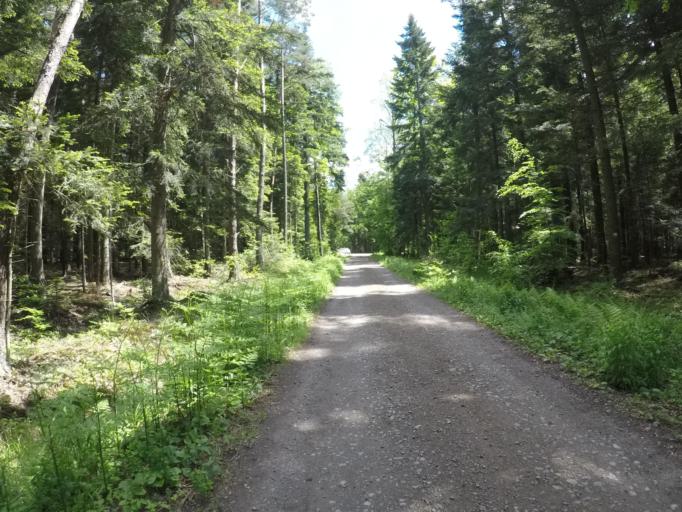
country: PL
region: Swietokrzyskie
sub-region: Powiat kielecki
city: Kostomloty Pierwsze
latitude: 50.9175
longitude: 20.6402
